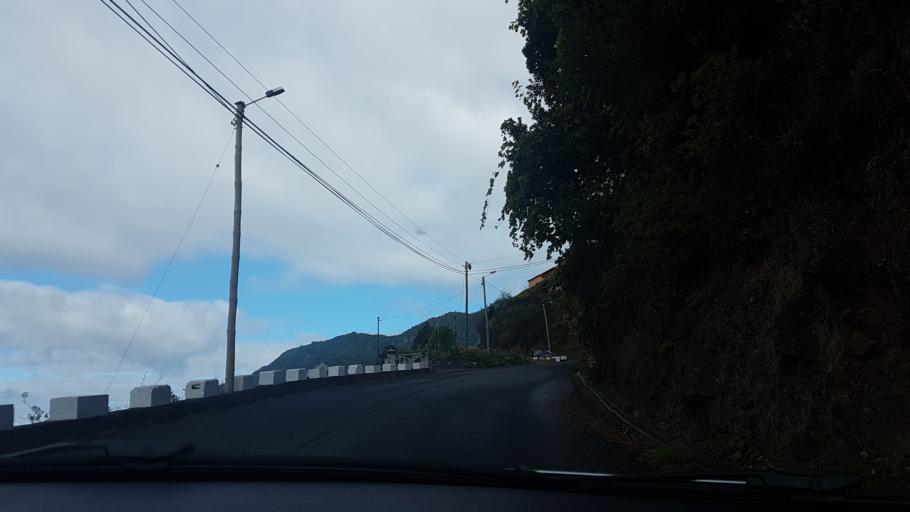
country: PT
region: Madeira
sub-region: Sao Vicente
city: Sao Vicente
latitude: 32.7806
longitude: -17.0306
